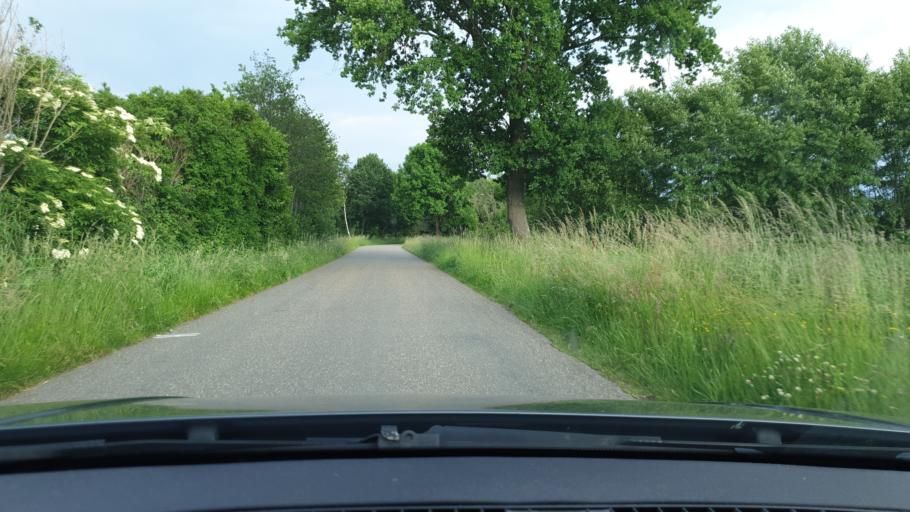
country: BE
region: Flanders
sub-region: Provincie Antwerpen
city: Geel
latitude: 51.1359
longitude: 4.9719
